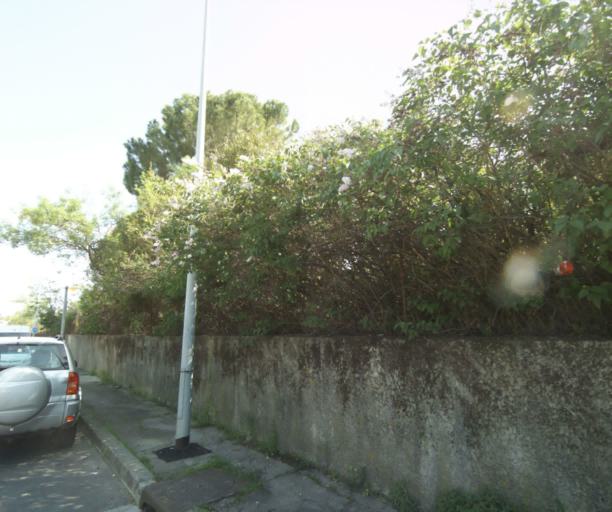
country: FR
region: Languedoc-Roussillon
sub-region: Departement de l'Herault
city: Montferrier-sur-Lez
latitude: 43.6409
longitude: 3.8354
